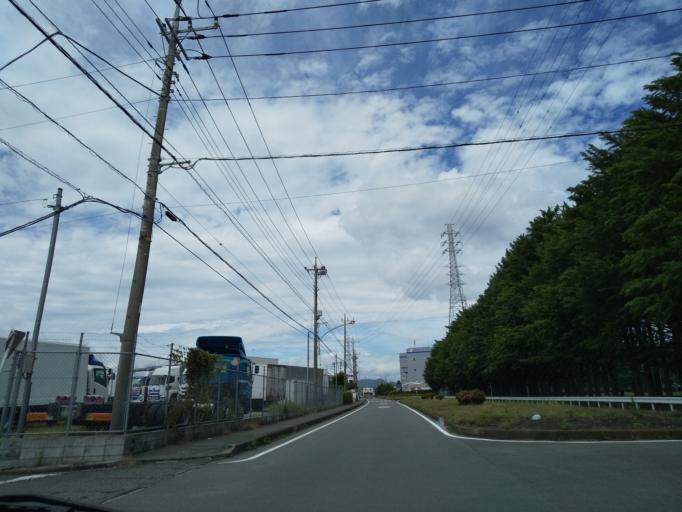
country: JP
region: Kanagawa
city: Zama
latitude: 35.5094
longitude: 139.3450
